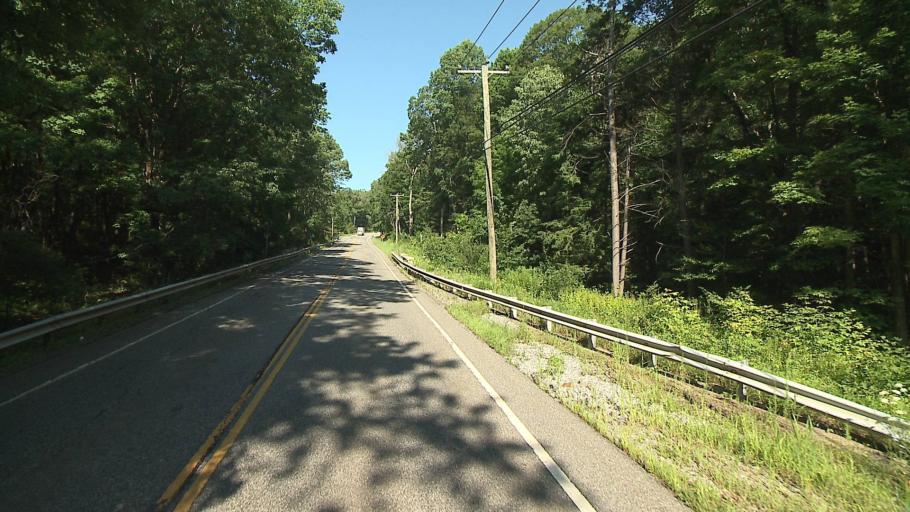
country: US
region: Connecticut
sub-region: Litchfield County
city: Kent
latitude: 41.8262
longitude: -73.4186
